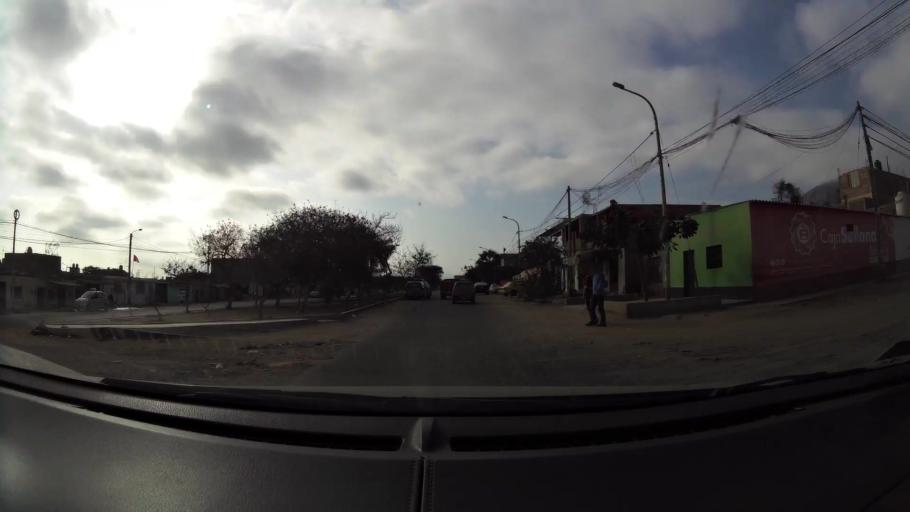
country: PE
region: La Libertad
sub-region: Provincia de Trujillo
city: La Esperanza
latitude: -8.0761
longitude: -79.0453
